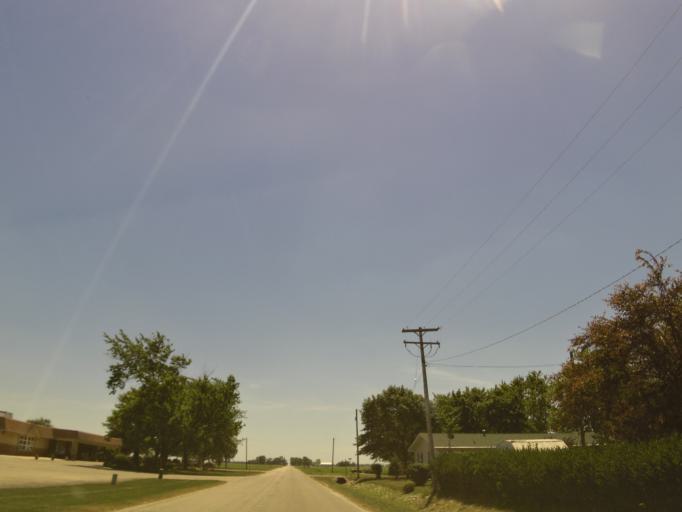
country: US
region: Illinois
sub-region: Livingston County
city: Chatsworth
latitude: 40.7531
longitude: -88.1827
